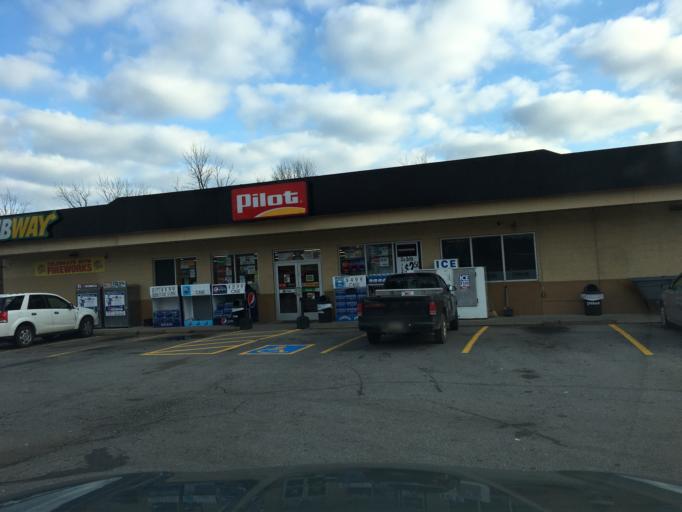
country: US
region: Tennessee
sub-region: Roane County
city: Kingston
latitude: 35.8741
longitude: -84.4593
